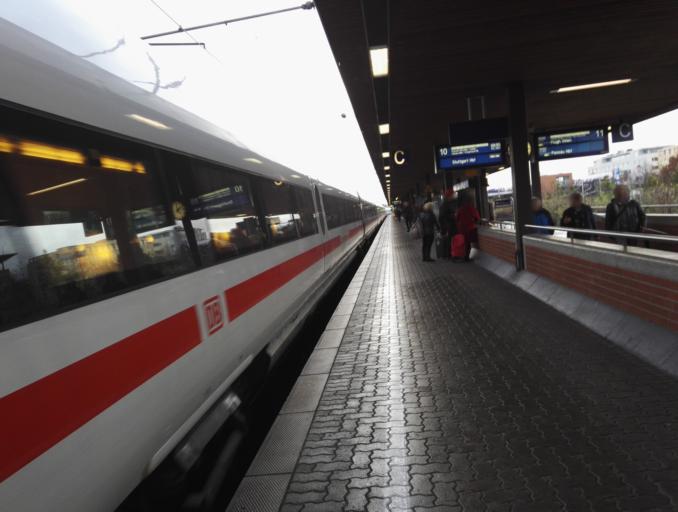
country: DE
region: Lower Saxony
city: Goettingen
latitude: 51.5367
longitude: 9.9255
